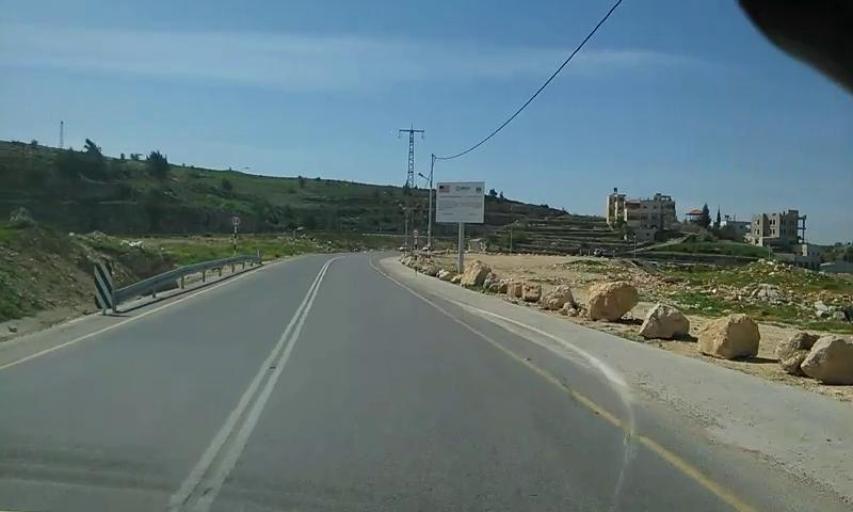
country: PS
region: West Bank
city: Battir
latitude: 31.7075
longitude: 35.1519
